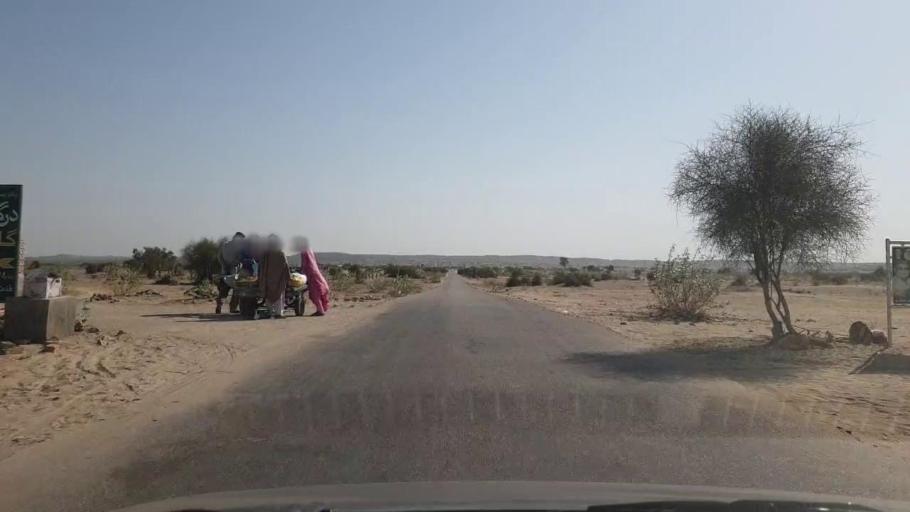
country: PK
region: Sindh
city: Chor
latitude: 25.4878
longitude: 69.7919
